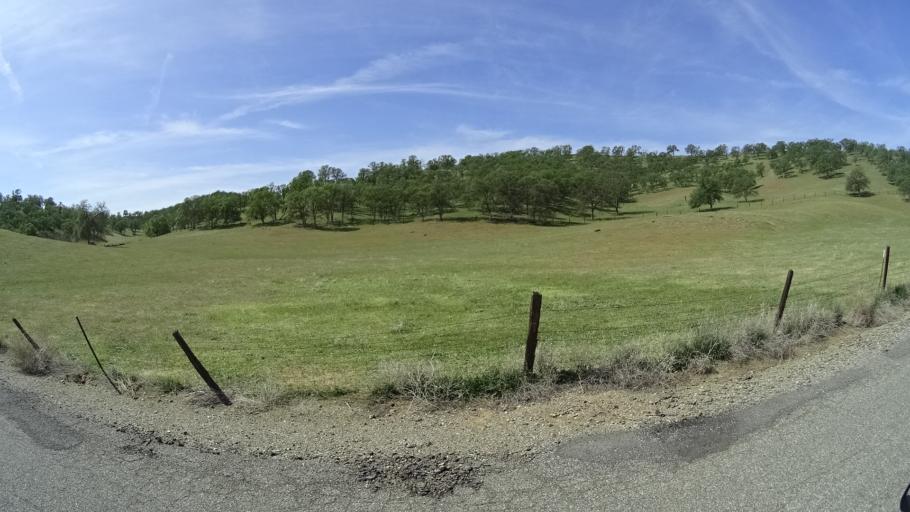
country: US
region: California
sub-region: Glenn County
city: Willows
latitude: 39.5526
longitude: -122.4333
